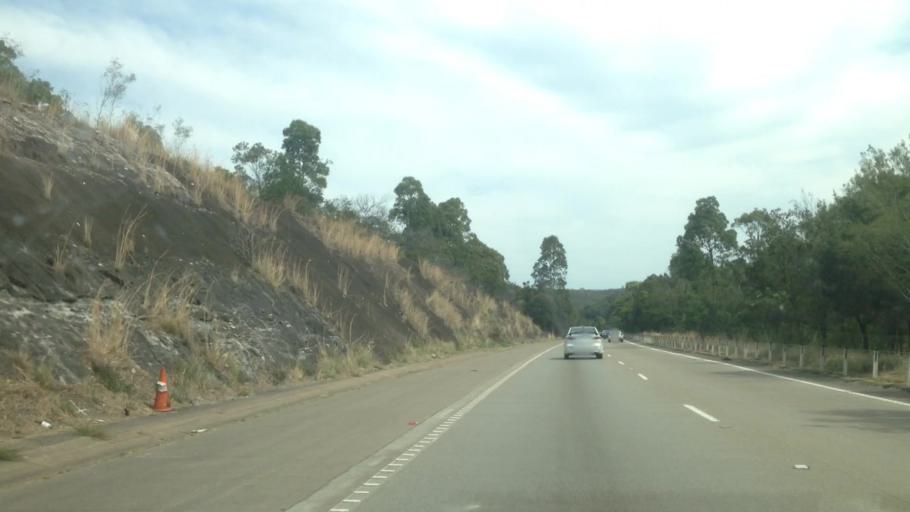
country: AU
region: New South Wales
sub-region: Lake Macquarie Shire
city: Fennell Bay
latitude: -32.9797
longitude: 151.5271
